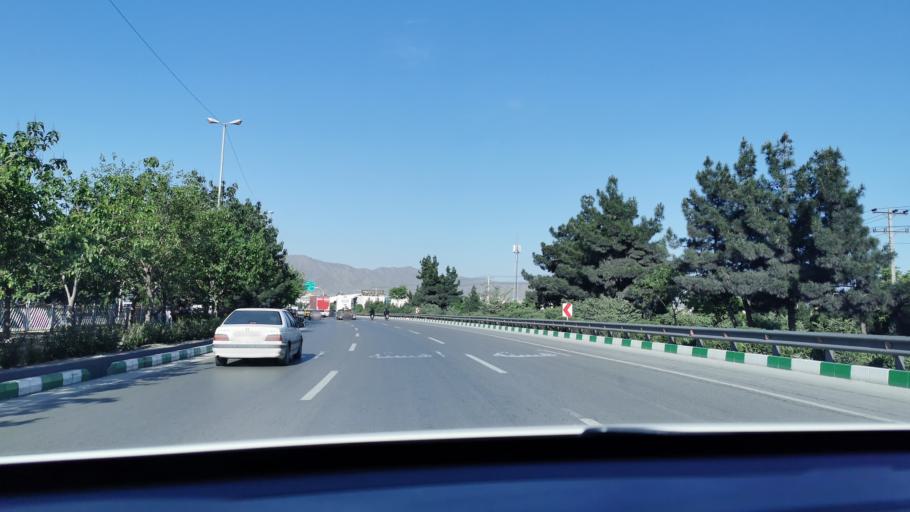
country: IR
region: Razavi Khorasan
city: Mashhad
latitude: 36.2581
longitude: 59.6247
